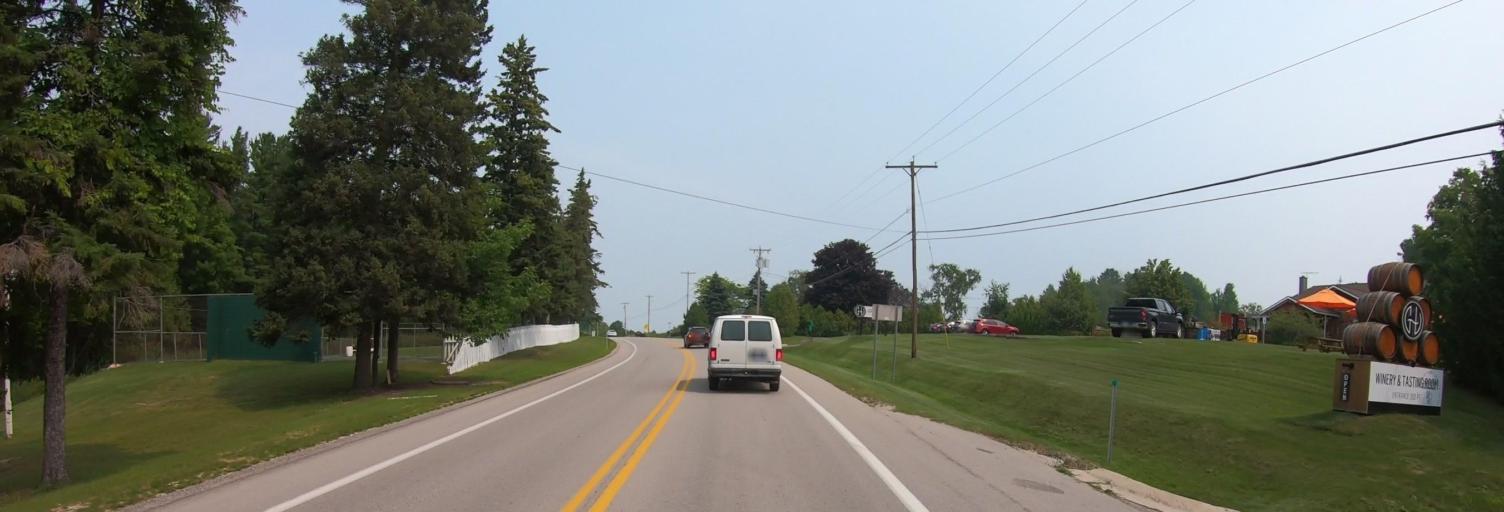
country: US
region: Michigan
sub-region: Leelanau County
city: Leland
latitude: 44.9828
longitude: -85.7744
